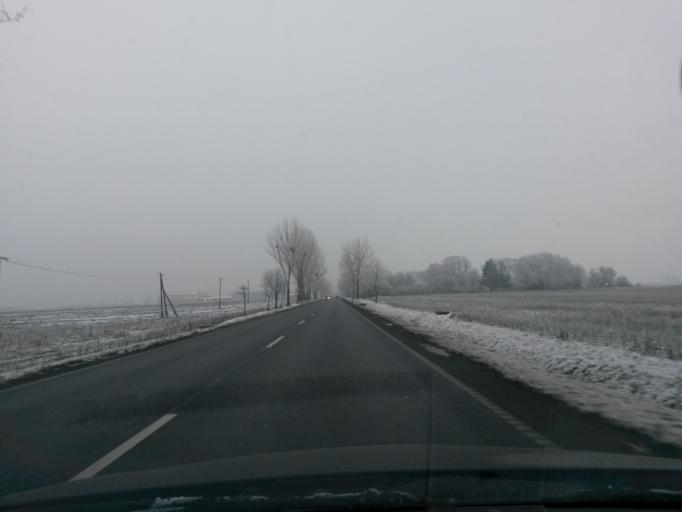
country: PL
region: Kujawsko-Pomorskie
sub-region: Powiat inowroclawski
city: Inowroclaw
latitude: 52.8184
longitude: 18.2940
